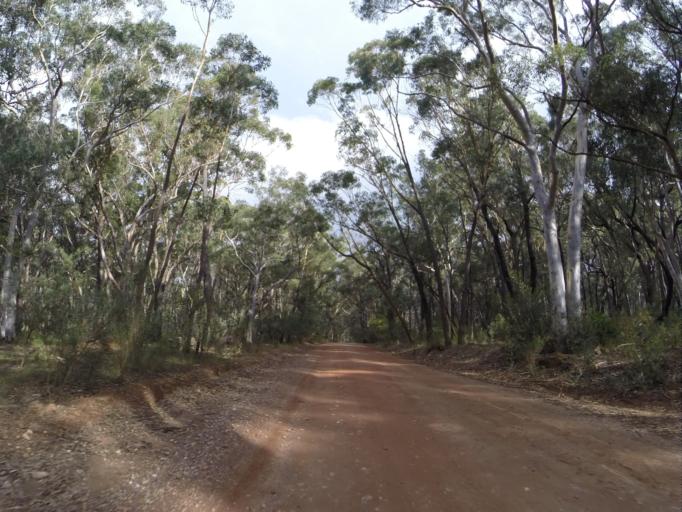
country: AU
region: New South Wales
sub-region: Wingecarribee
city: Bundanoon
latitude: -34.5280
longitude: 150.2138
